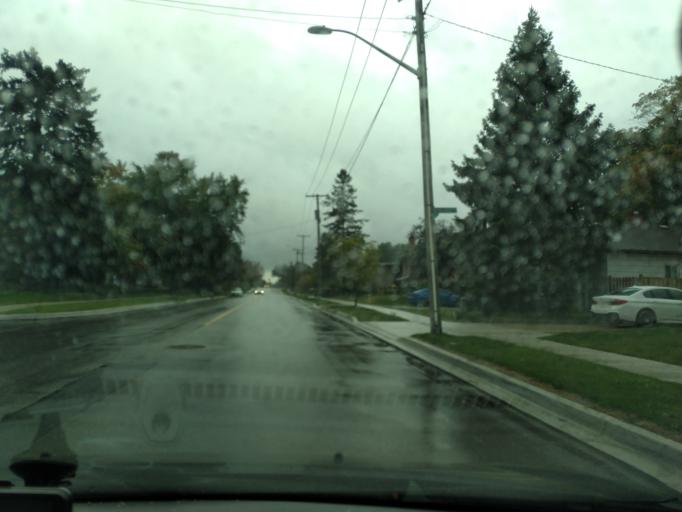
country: CA
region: Ontario
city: Barrie
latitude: 44.4020
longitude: -79.6752
